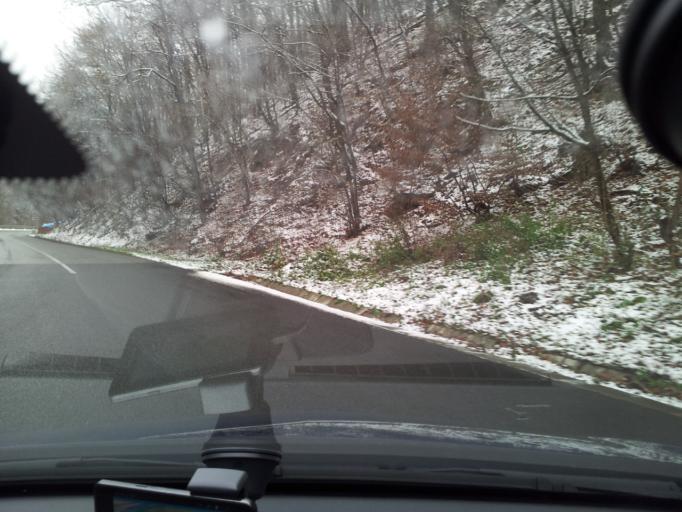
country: SK
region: Presovsky
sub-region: Okres Presov
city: Presov
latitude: 48.8574
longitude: 21.2289
